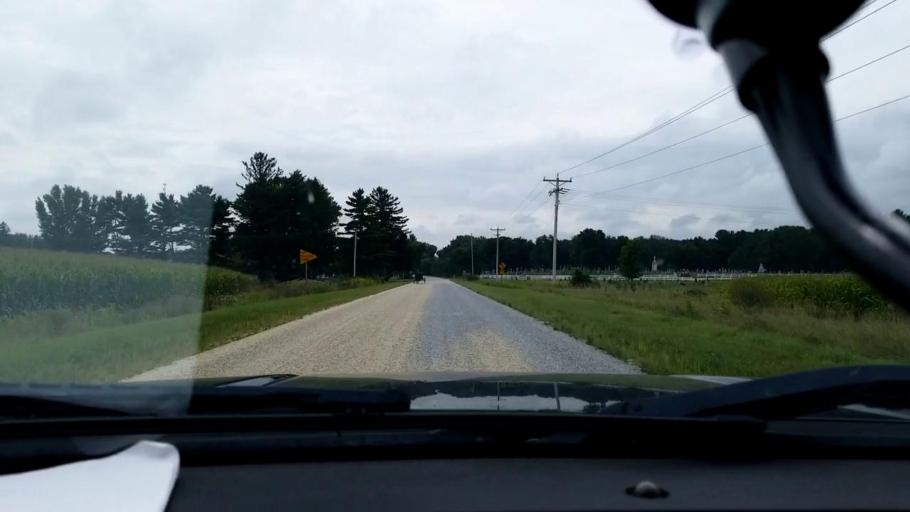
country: US
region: Iowa
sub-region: Fayette County
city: Oelwein
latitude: 42.6058
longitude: -91.9044
